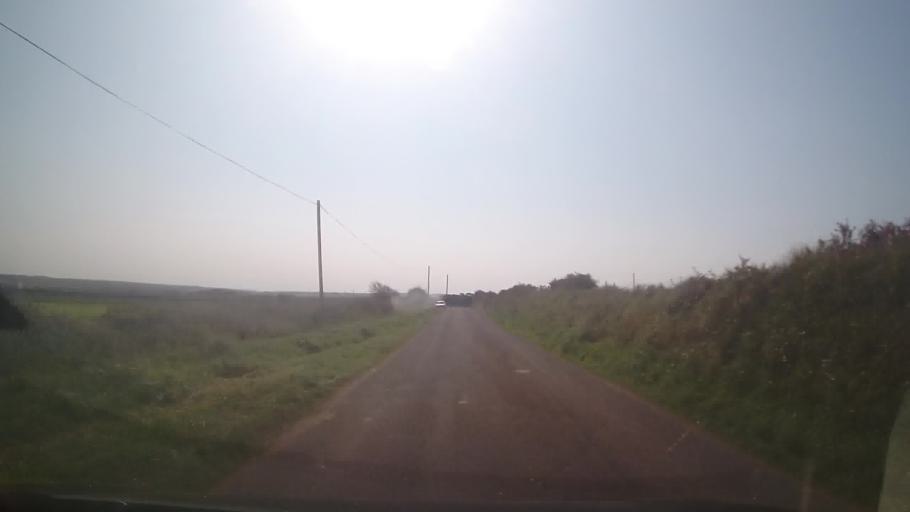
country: GB
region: Wales
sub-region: Pembrokeshire
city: Saint David's
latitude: 51.9133
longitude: -5.2400
